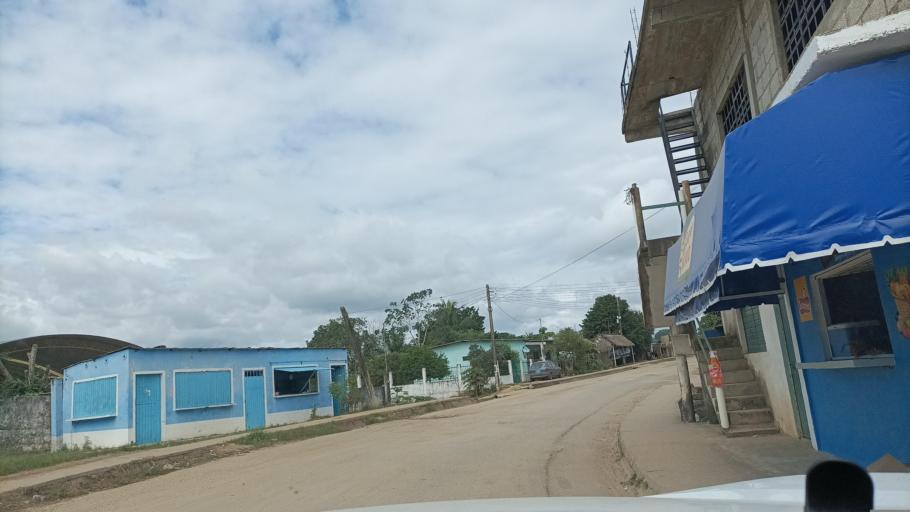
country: MX
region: Veracruz
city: Texistepec
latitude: 17.9596
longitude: -94.8135
